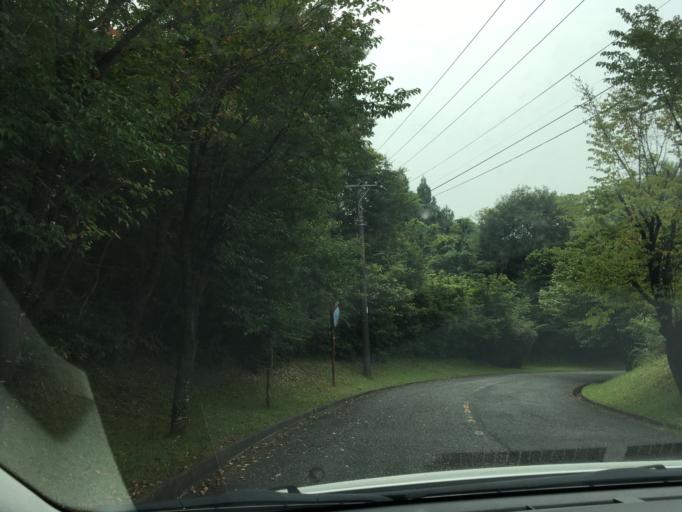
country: JP
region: Iwate
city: Ichinoseki
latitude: 38.8784
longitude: 141.0736
